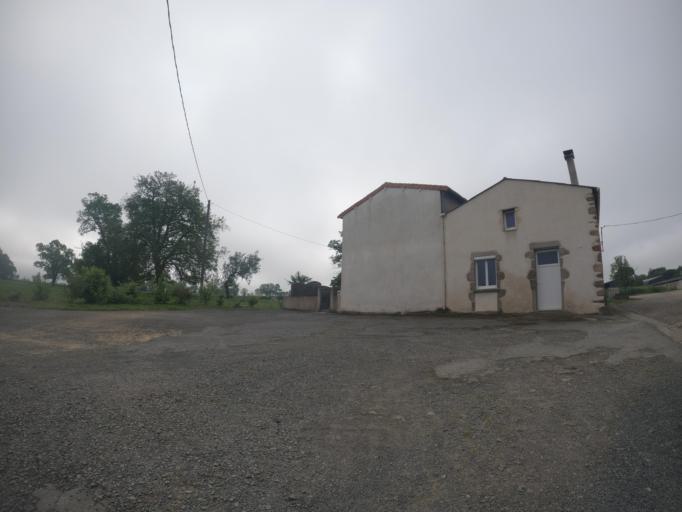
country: FR
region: Poitou-Charentes
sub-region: Departement des Deux-Sevres
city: Saint-Varent
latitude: 46.8822
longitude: -0.3158
